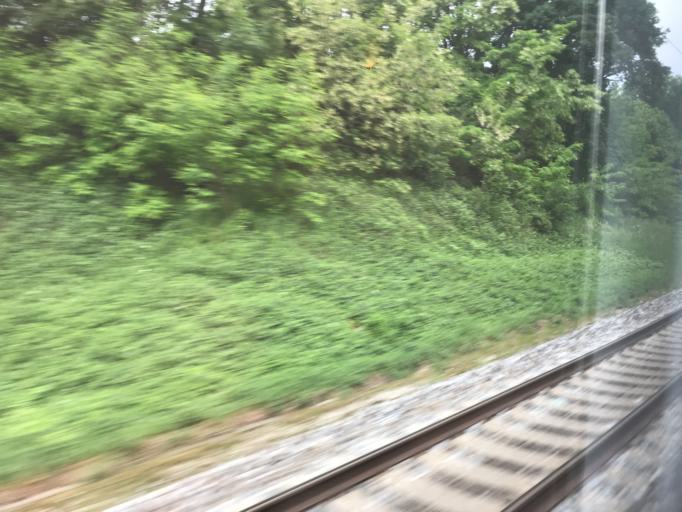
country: DE
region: Bavaria
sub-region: Swabia
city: Dinkelscherben
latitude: 48.3692
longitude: 10.5646
